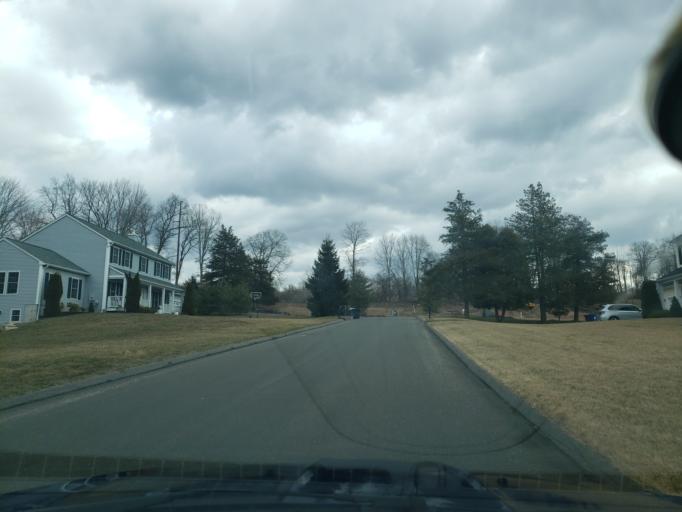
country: US
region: Connecticut
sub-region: Fairfield County
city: Bethel
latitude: 41.3899
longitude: -73.3813
